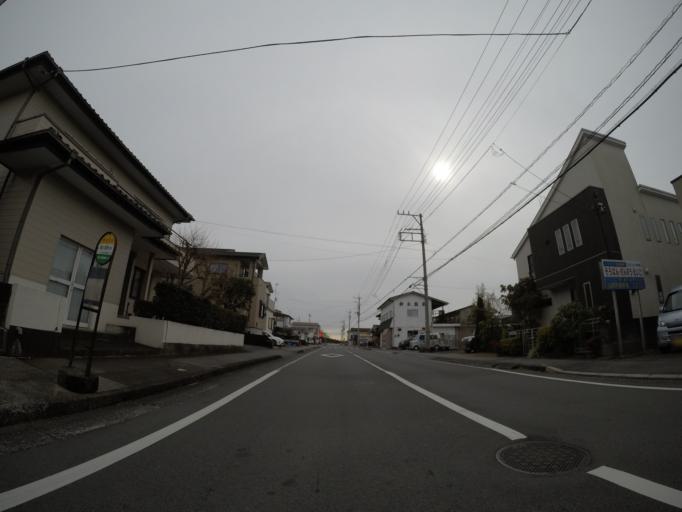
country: JP
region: Shizuoka
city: Fujinomiya
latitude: 35.2504
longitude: 138.6375
